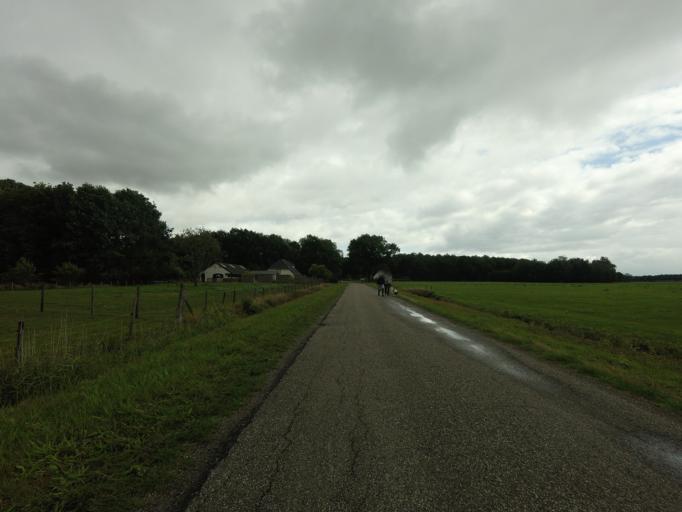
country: NL
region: Drenthe
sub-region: Gemeente Westerveld
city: Dwingeloo
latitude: 52.9785
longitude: 6.3066
